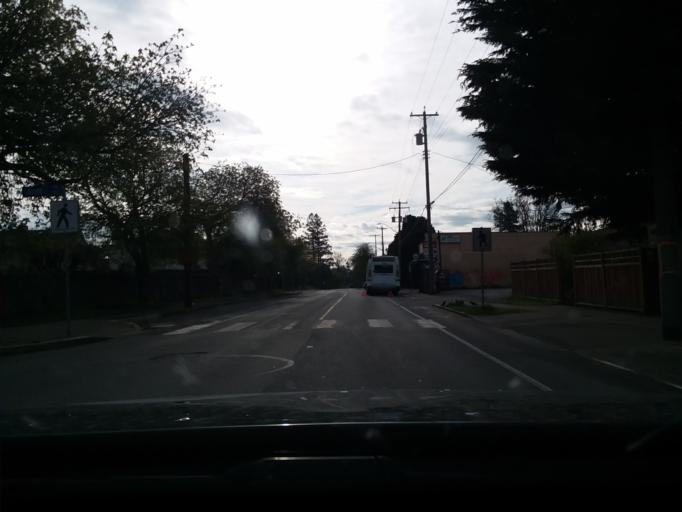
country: CA
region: British Columbia
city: Victoria
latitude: 48.4398
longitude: -123.3941
